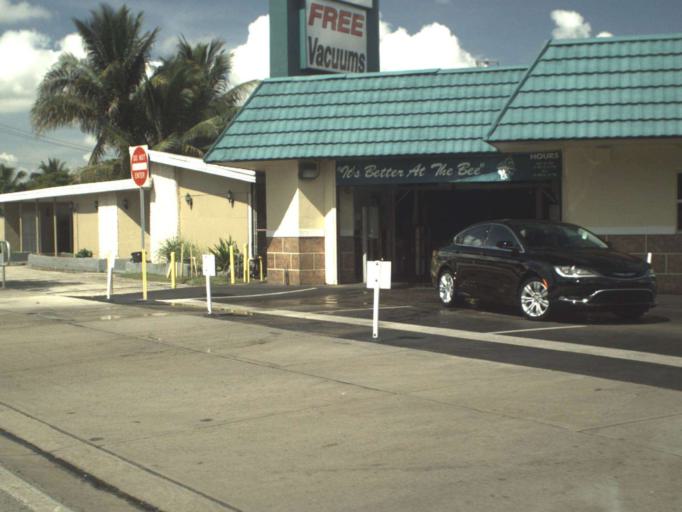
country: US
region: Florida
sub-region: Miami-Dade County
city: Biscayne Park
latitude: 25.8724
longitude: -80.1724
